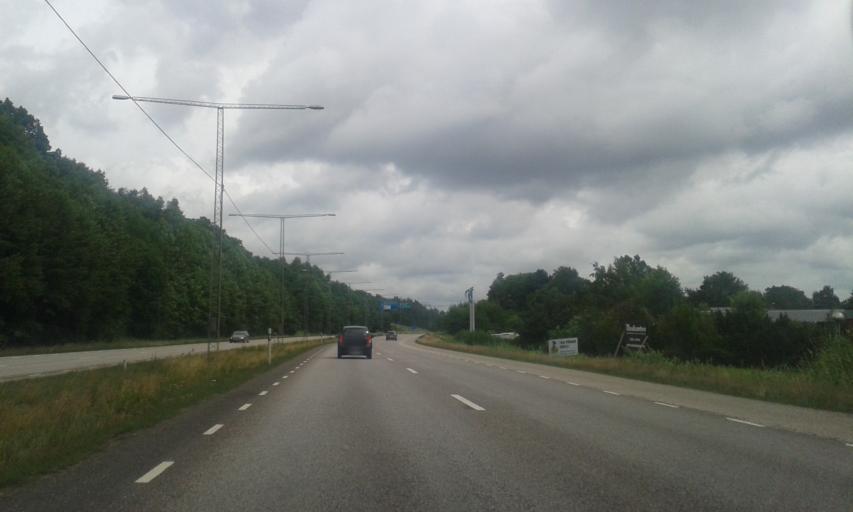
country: SE
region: Vaestra Goetaland
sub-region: Kungalvs Kommun
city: Kungalv
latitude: 57.8730
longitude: 11.9523
